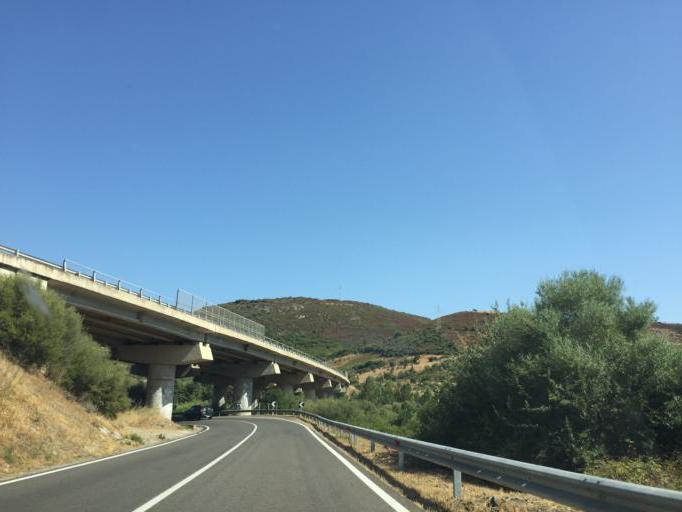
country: IT
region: Sardinia
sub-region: Provincia di Olbia-Tempio
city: San Teodoro
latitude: 40.7311
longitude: 9.6496
